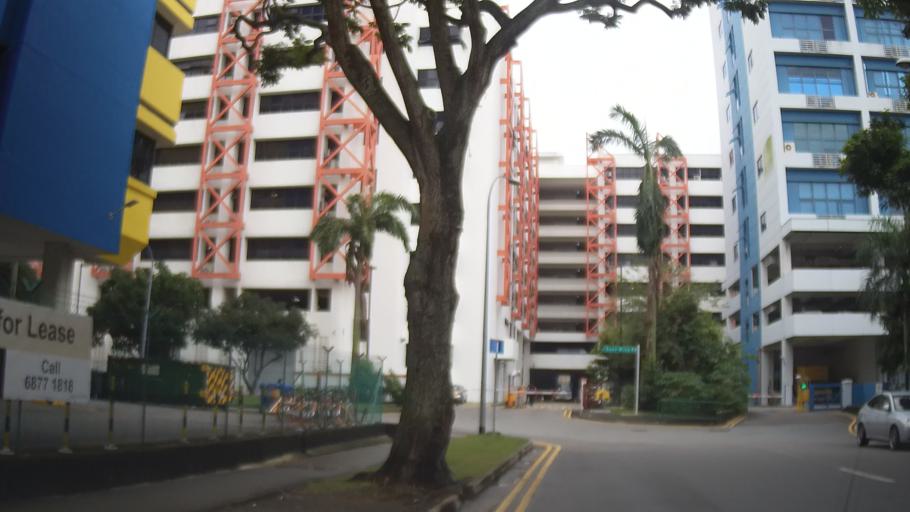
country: SG
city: Singapore
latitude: 1.3267
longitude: 103.8788
